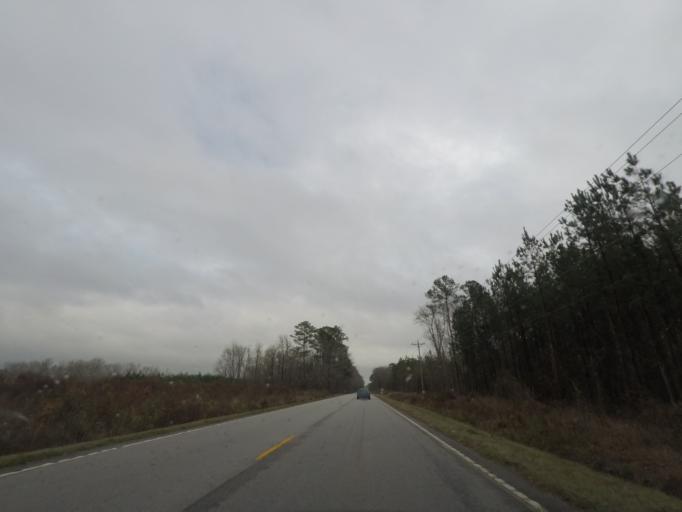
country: US
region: South Carolina
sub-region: Colleton County
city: Walterboro
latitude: 32.8126
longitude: -80.5312
